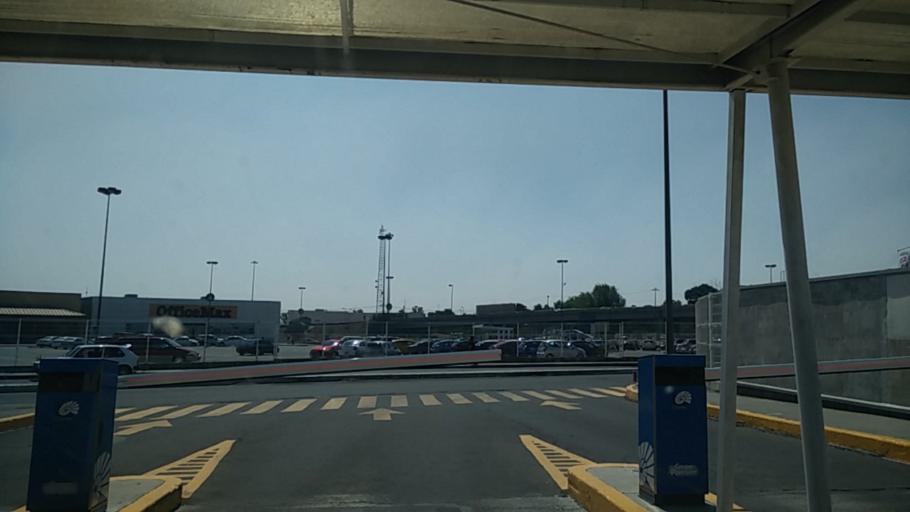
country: MX
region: Mexico
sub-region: Atenco
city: Colonia el Salado
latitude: 19.5813
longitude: -99.0231
